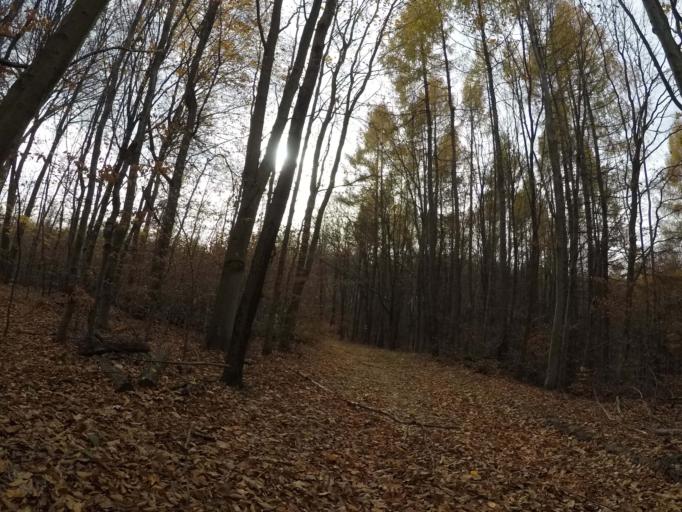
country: SK
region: Presovsky
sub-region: Okres Presov
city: Presov
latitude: 48.9647
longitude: 21.1829
